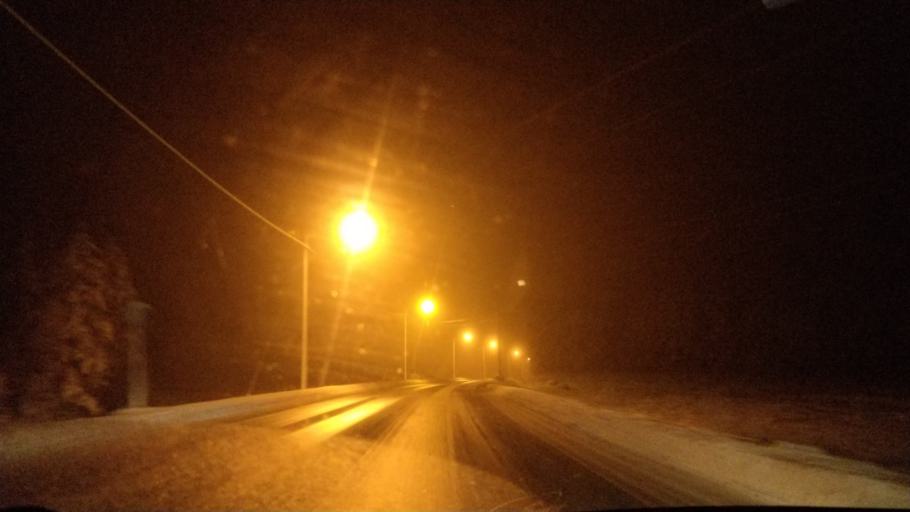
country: FI
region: Lapland
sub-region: Rovaniemi
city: Rovaniemi
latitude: 66.4451
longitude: 25.5617
